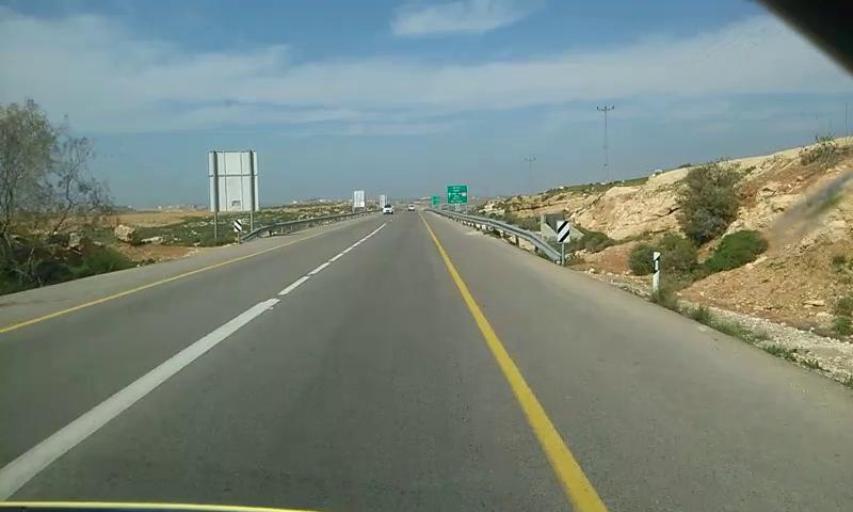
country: PS
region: West Bank
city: Az Zahiriyah
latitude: 31.3802
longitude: 35.0046
